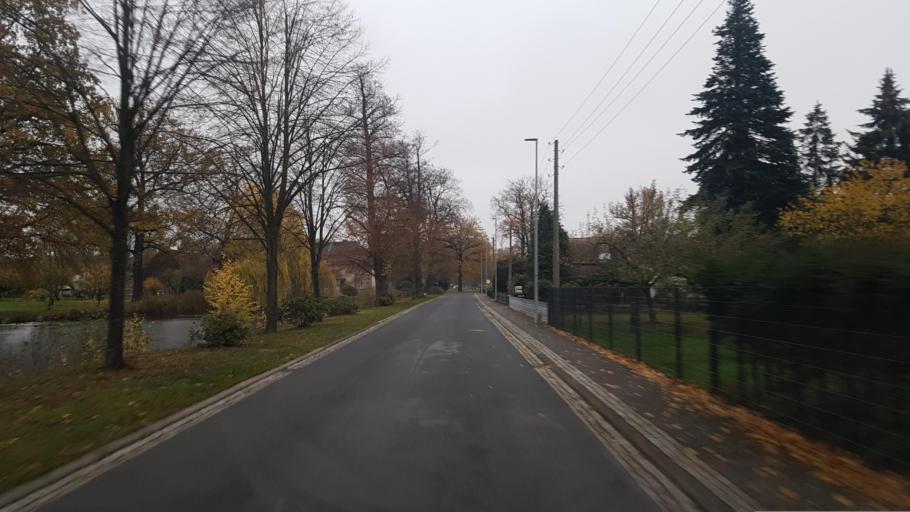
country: DE
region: Brandenburg
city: Hermsdorf
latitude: 51.4039
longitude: 13.8967
